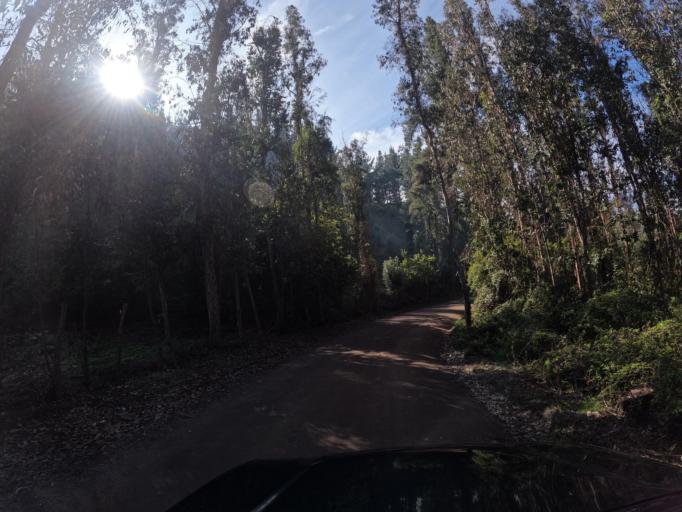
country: CL
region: Biobio
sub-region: Provincia de Concepcion
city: Chiguayante
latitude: -37.0661
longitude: -72.8990
